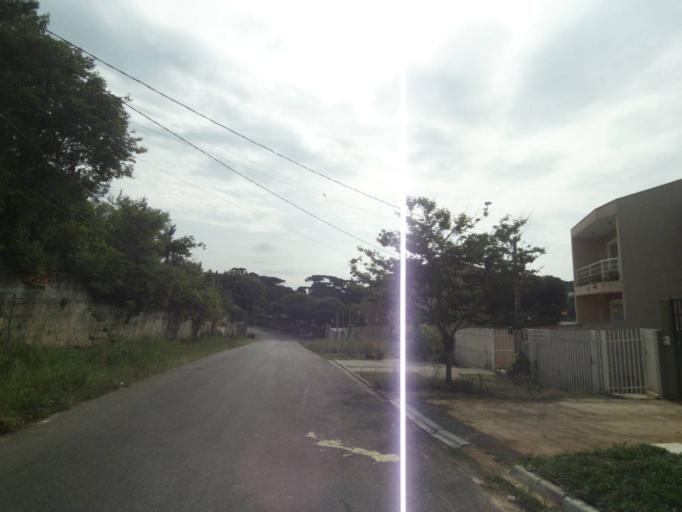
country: BR
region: Parana
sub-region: Curitiba
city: Curitiba
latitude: -25.4102
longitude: -49.3029
